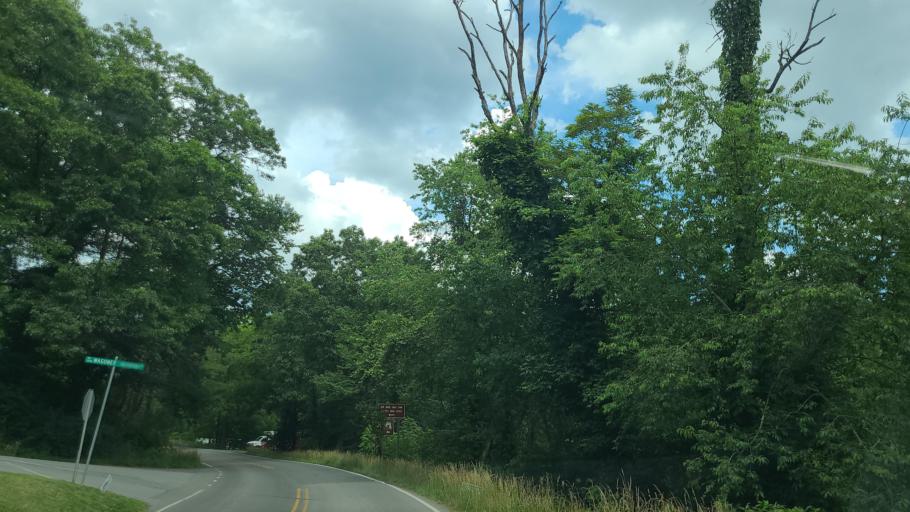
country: US
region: North Carolina
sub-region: Ashe County
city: Jefferson
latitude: 36.4013
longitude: -81.3884
